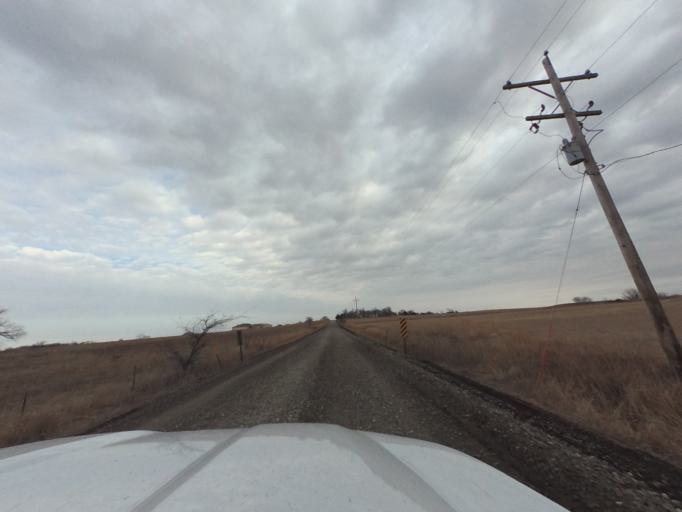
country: US
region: Kansas
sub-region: Chase County
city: Cottonwood Falls
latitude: 38.4441
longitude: -96.3731
